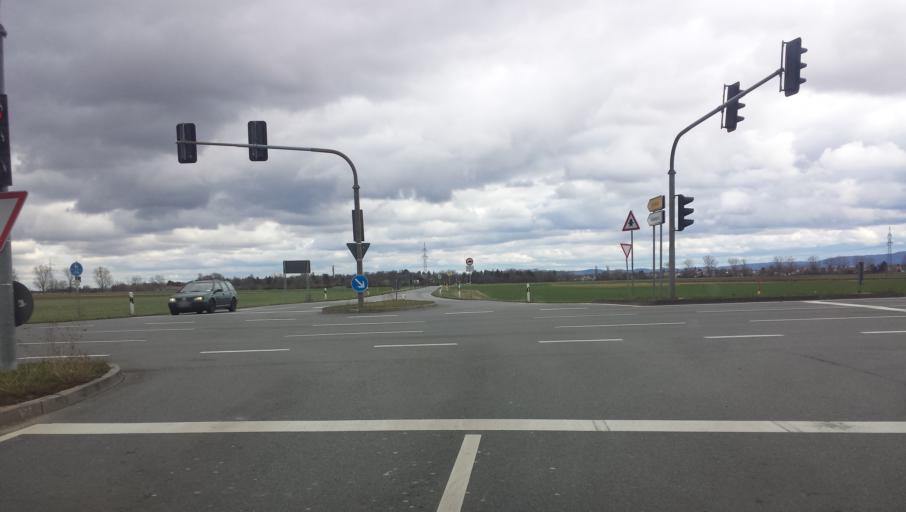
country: DE
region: Hesse
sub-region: Regierungsbezirk Darmstadt
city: Stockstadt am Rhein
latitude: 49.8135
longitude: 8.4830
